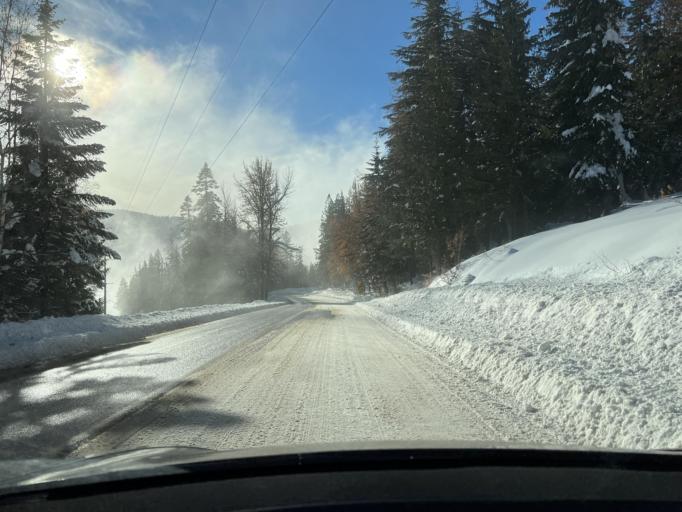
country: US
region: Idaho
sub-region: Bonner County
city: Ponderay
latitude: 48.3414
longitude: -116.6014
